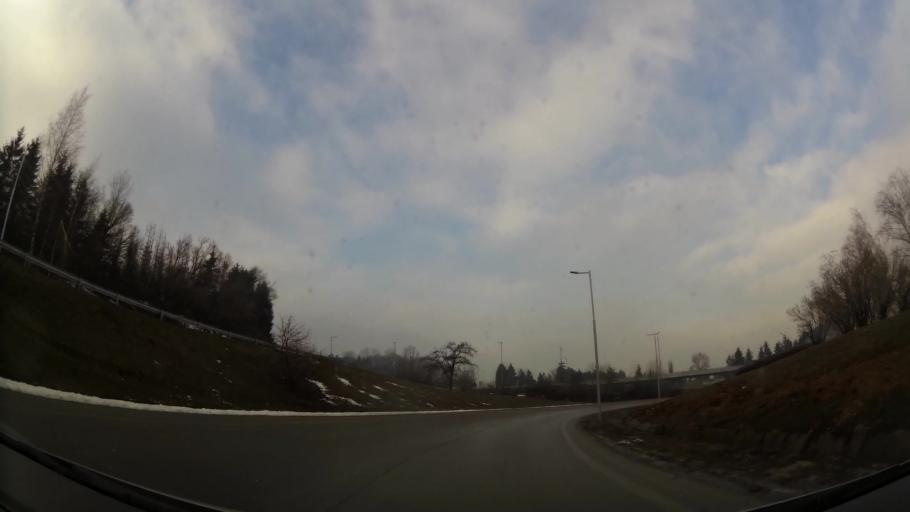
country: BG
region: Sofia-Capital
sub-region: Stolichna Obshtina
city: Sofia
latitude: 42.6523
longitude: 23.2834
